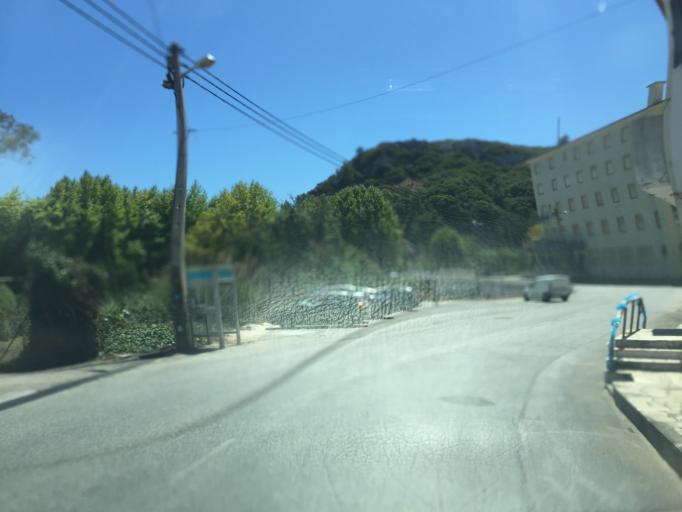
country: PT
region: Lisbon
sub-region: Torres Vedras
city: A dos Cunhados
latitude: 39.1833
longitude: -9.3266
